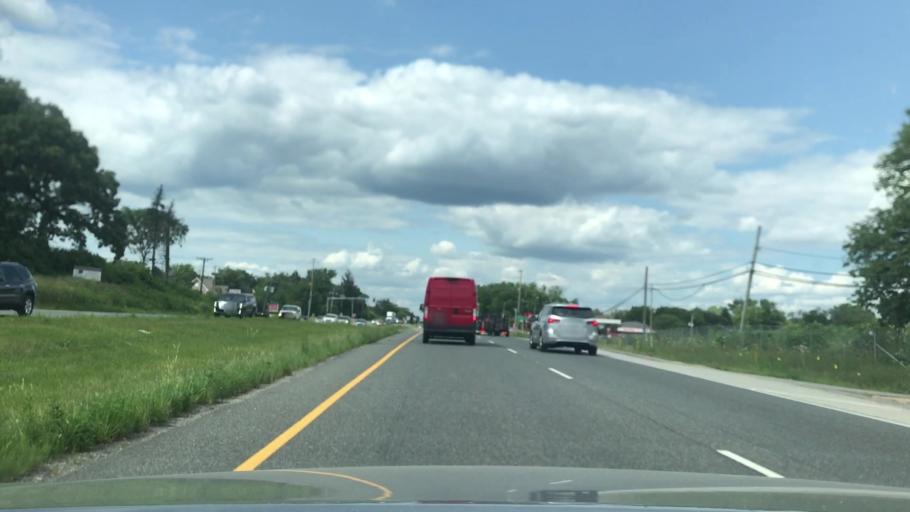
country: US
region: Illinois
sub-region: DuPage County
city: Burr Ridge
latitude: 41.7212
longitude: -87.9436
